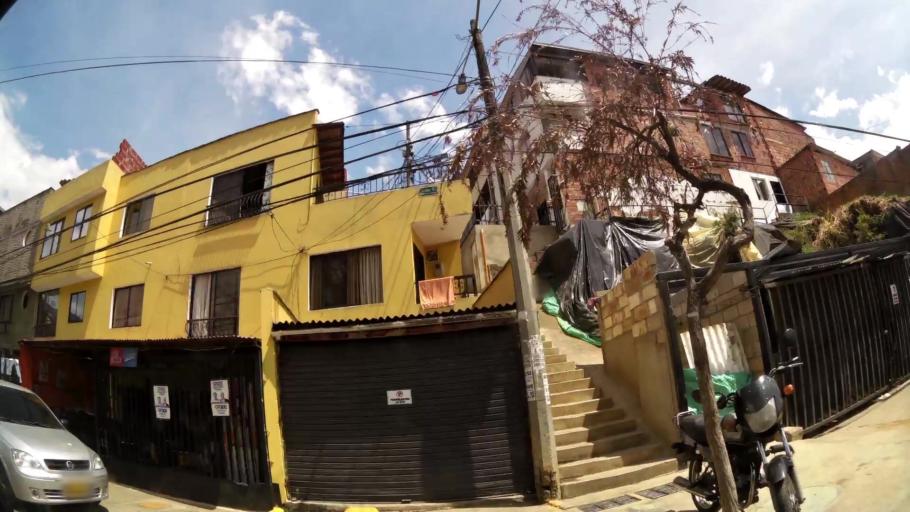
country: CO
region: Antioquia
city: Bello
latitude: 6.3477
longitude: -75.5534
